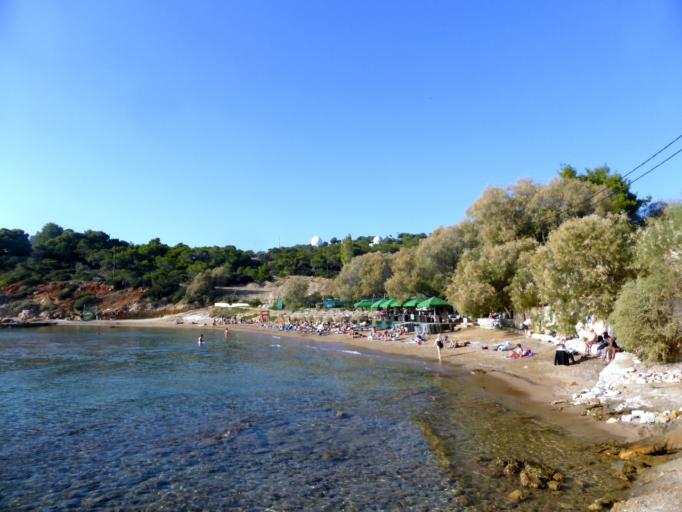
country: GR
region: Attica
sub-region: Nomarchia Anatolikis Attikis
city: Vouliagmeni
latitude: 37.8135
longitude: 23.7698
